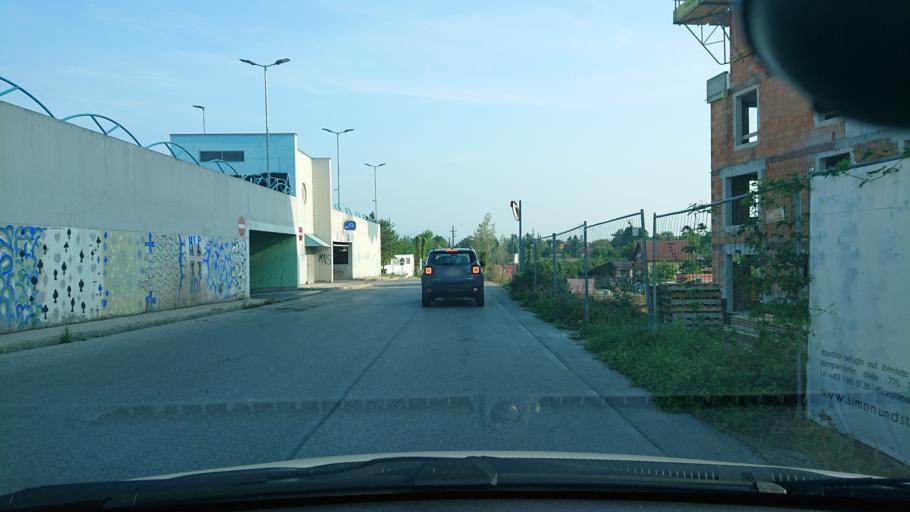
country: AT
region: Lower Austria
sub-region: Politischer Bezirk Baden
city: Kottingbrunn
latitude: 47.9377
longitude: 16.2323
